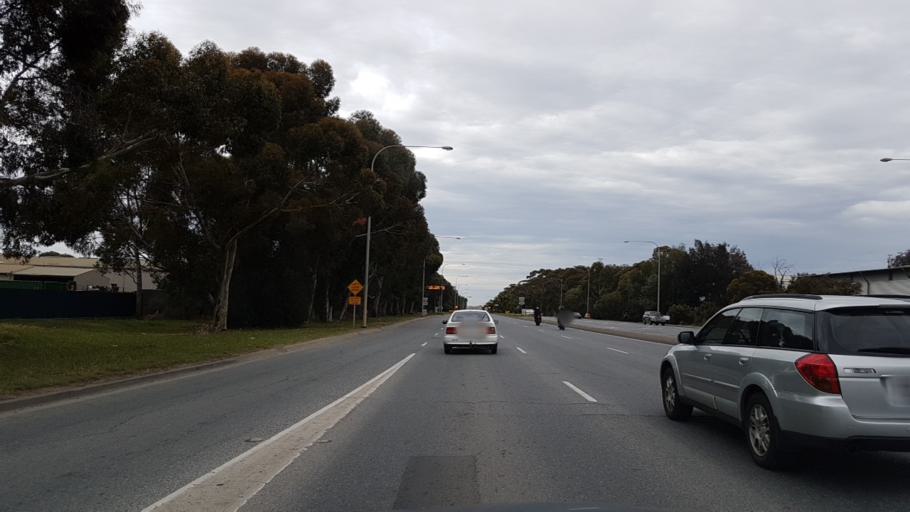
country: AU
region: South Australia
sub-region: Port Adelaide Enfield
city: Enfield
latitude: -34.8271
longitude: 138.5984
